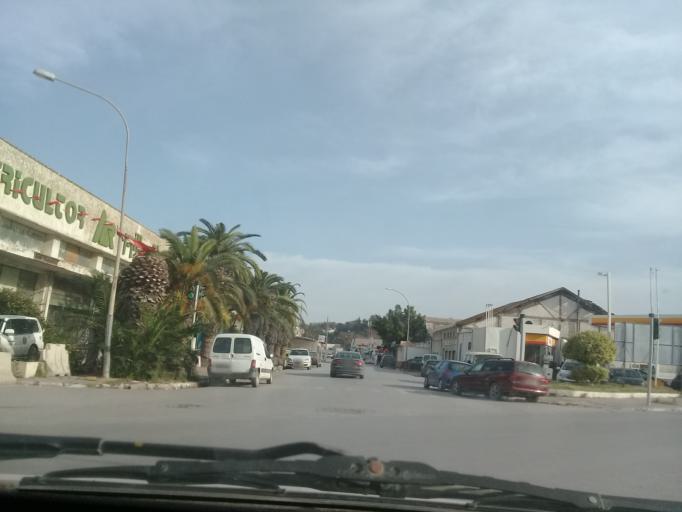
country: TN
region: Tunis
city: Tunis
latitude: 36.7942
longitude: 10.1872
